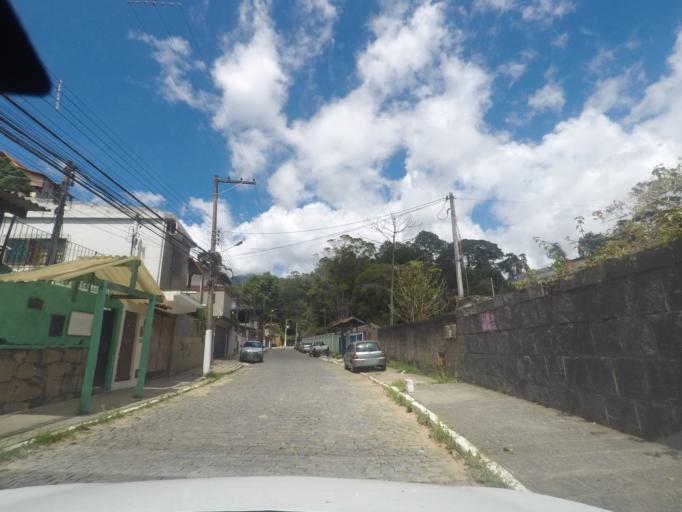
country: BR
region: Rio de Janeiro
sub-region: Teresopolis
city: Teresopolis
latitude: -22.4109
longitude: -42.9847
